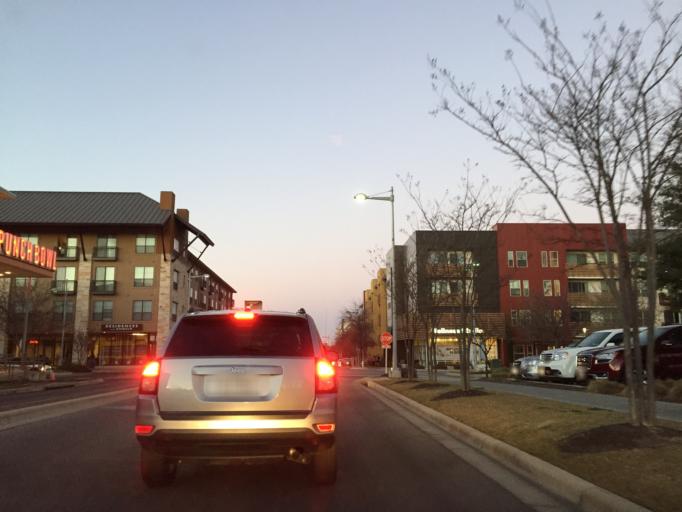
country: US
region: Texas
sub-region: Travis County
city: Wells Branch
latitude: 30.3999
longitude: -97.7252
